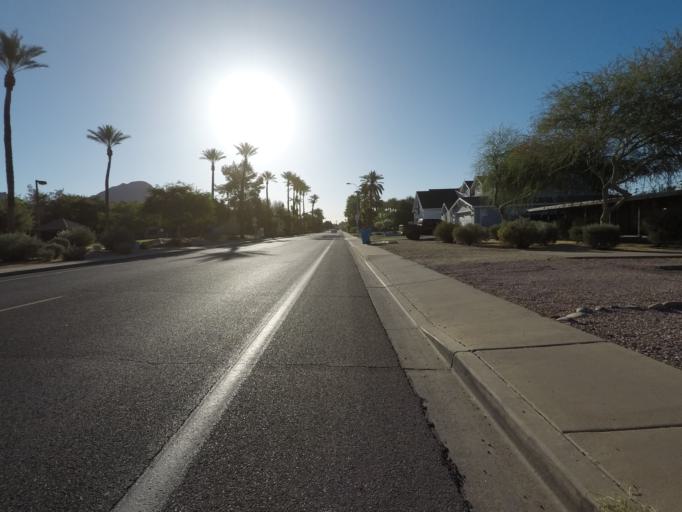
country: US
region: Arizona
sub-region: Maricopa County
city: Paradise Valley
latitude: 33.5023
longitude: -111.9906
